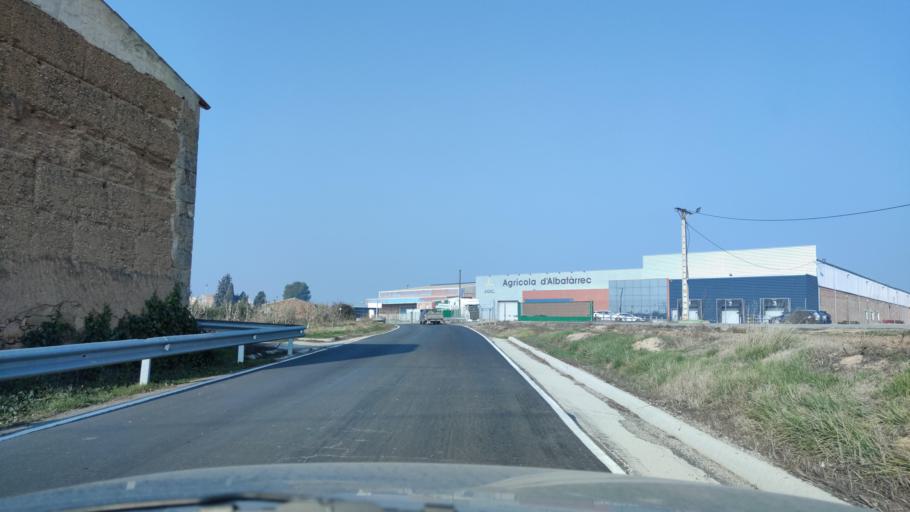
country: ES
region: Catalonia
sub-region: Provincia de Lleida
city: Lleida
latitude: 41.5706
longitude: 0.6096
